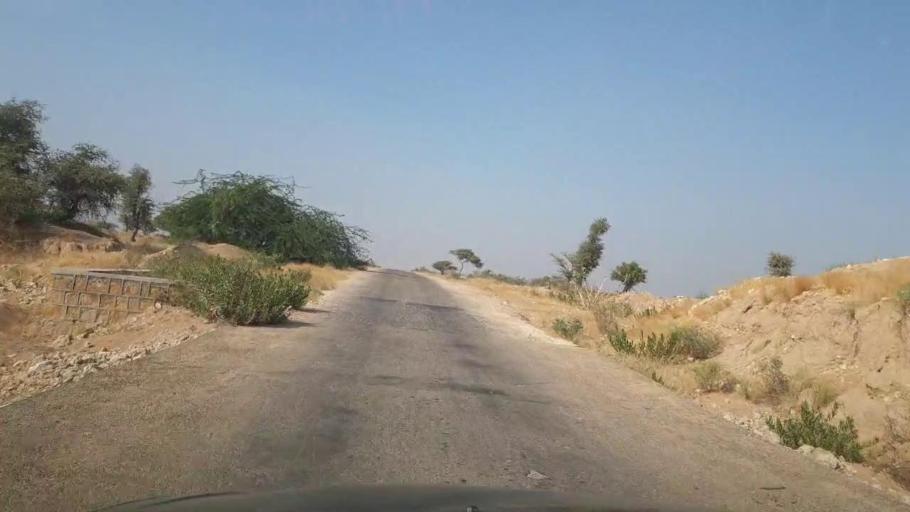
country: PK
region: Sindh
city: Jamshoro
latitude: 25.5783
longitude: 67.8220
